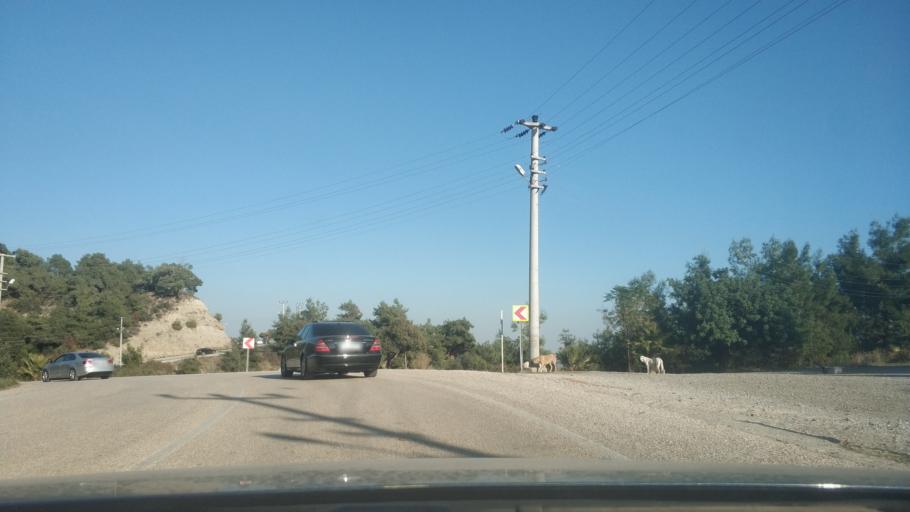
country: TR
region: Adana
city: Adana
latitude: 37.0987
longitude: 35.2884
